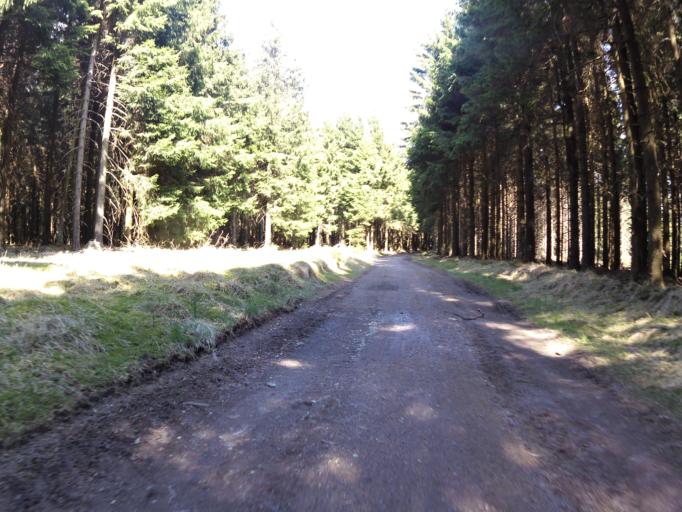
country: DE
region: Thuringia
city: Unterschonau
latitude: 50.7378
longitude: 10.6039
